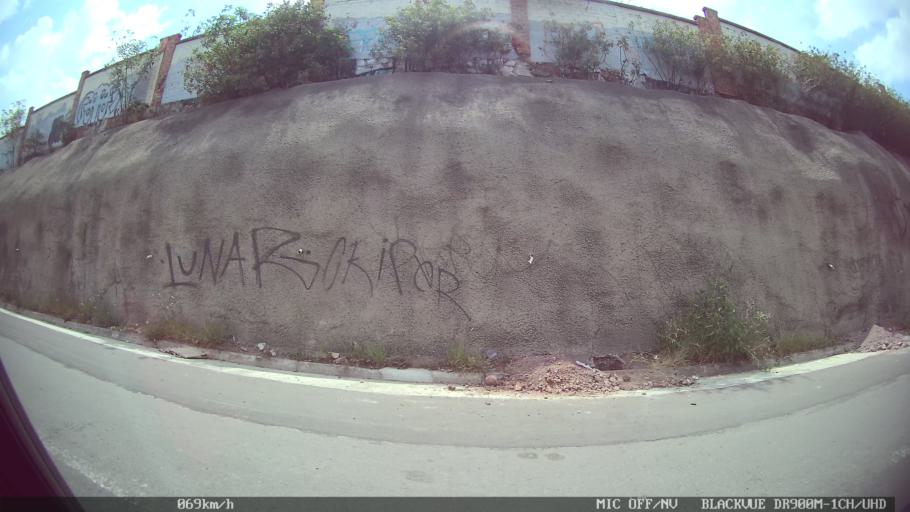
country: MX
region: Jalisco
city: Tonala
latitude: 20.6362
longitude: -103.2434
